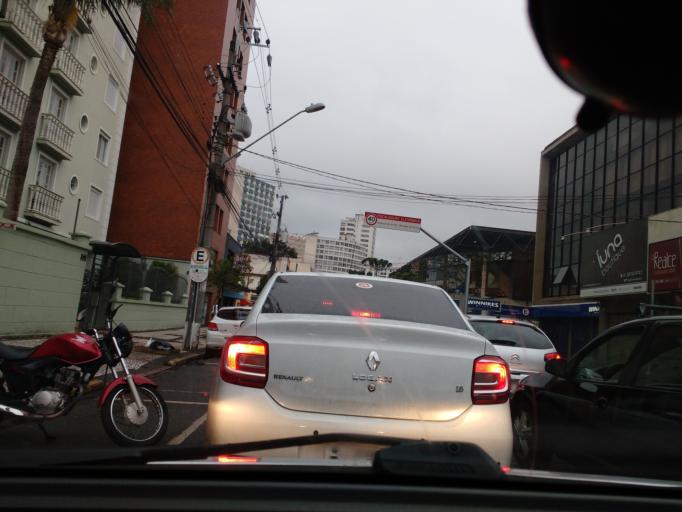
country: BR
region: Parana
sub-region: Curitiba
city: Curitiba
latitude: -25.4261
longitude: -49.2630
